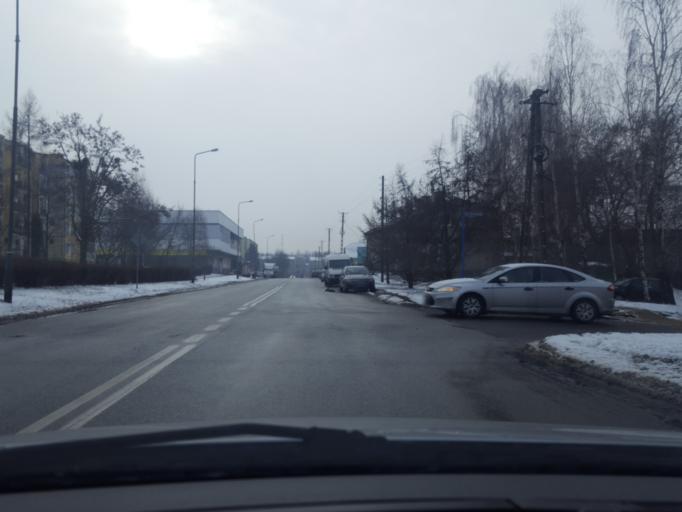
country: PL
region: Lodz Voivodeship
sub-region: Powiat brzezinski
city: Brzeziny
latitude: 51.8034
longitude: 19.7560
